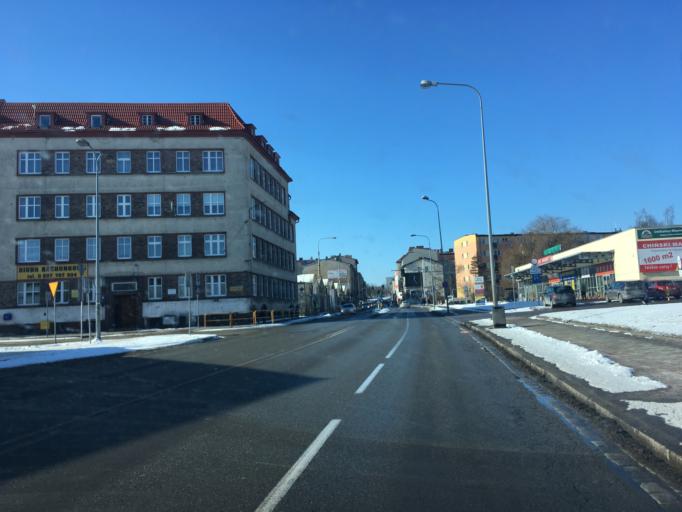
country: PL
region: Pomeranian Voivodeship
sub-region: Slupsk
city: Slupsk
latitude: 54.4709
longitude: 17.0261
